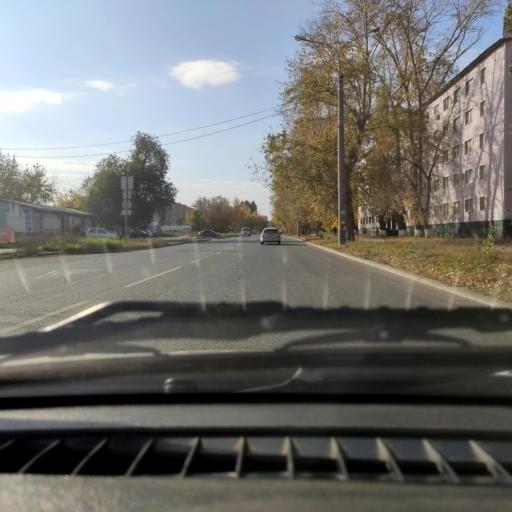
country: RU
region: Samara
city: Tol'yatti
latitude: 53.5290
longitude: 49.4308
